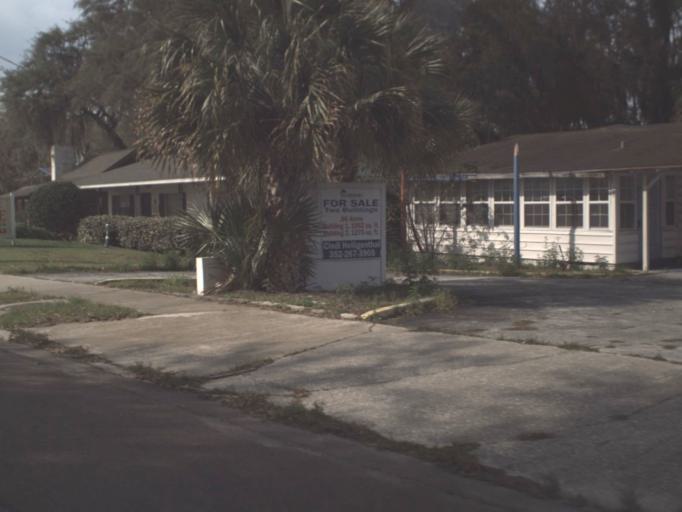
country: US
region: Florida
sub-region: Lake County
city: Eustis
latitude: 28.8627
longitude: -81.6851
